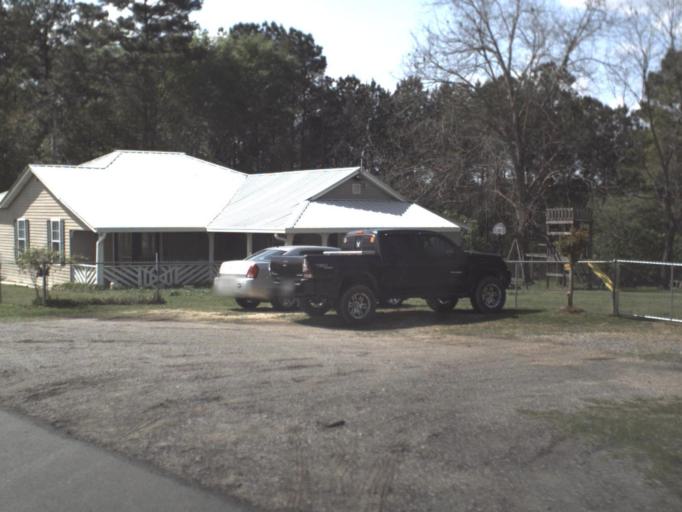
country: US
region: Alabama
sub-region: Covington County
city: Florala
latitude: 30.9668
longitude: -86.4049
